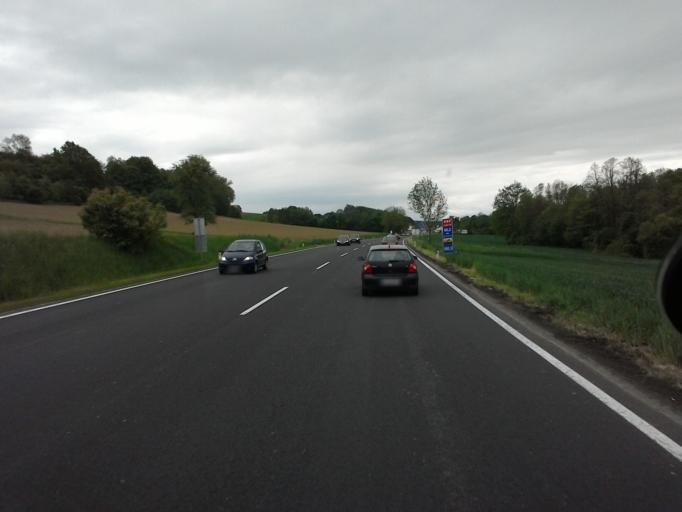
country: AT
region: Upper Austria
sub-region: Wels-Land
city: Thalheim bei Wels
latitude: 48.1481
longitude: 14.0456
